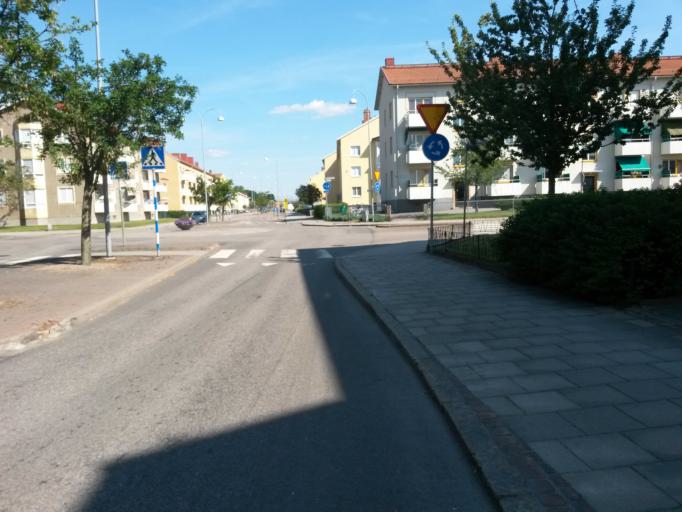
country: SE
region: Vaestra Goetaland
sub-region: Lidkopings Kommun
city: Lidkoping
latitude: 58.4993
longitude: 13.1663
